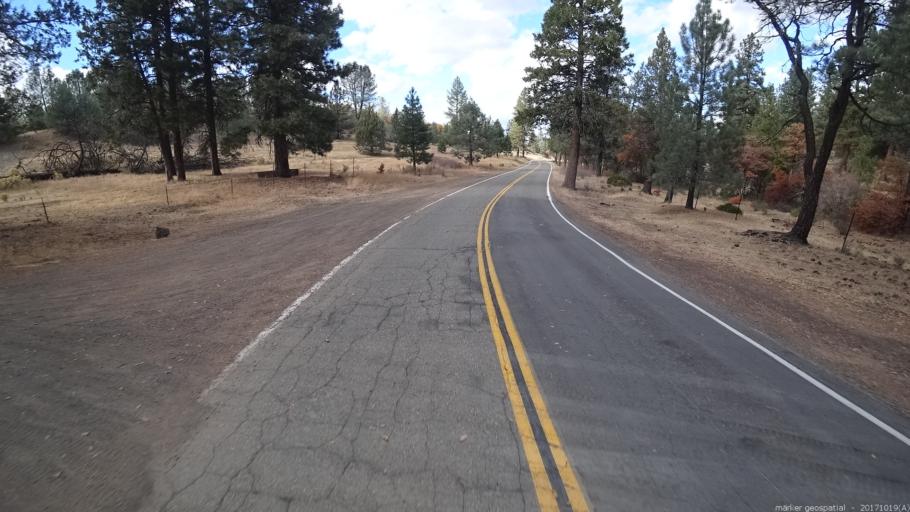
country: US
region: California
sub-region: Shasta County
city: Burney
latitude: 40.9467
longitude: -121.4414
